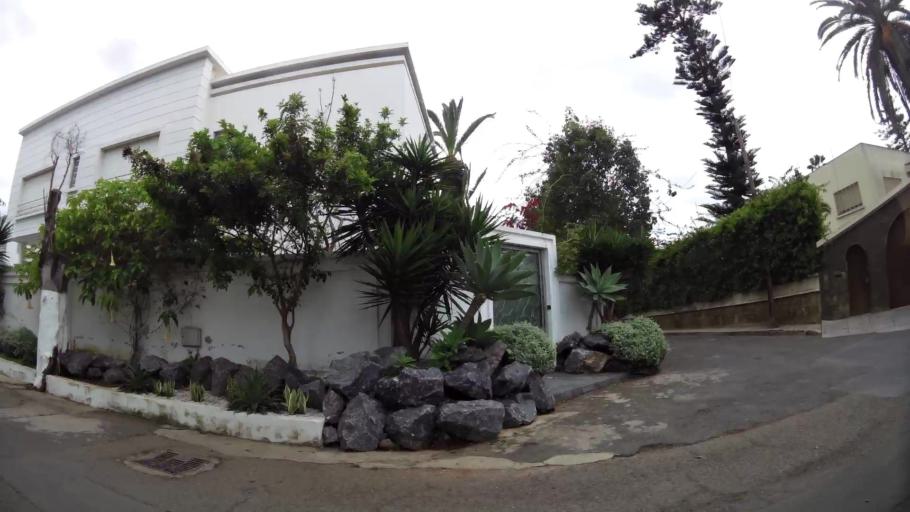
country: MA
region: Grand Casablanca
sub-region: Casablanca
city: Casablanca
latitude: 33.5621
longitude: -7.6337
